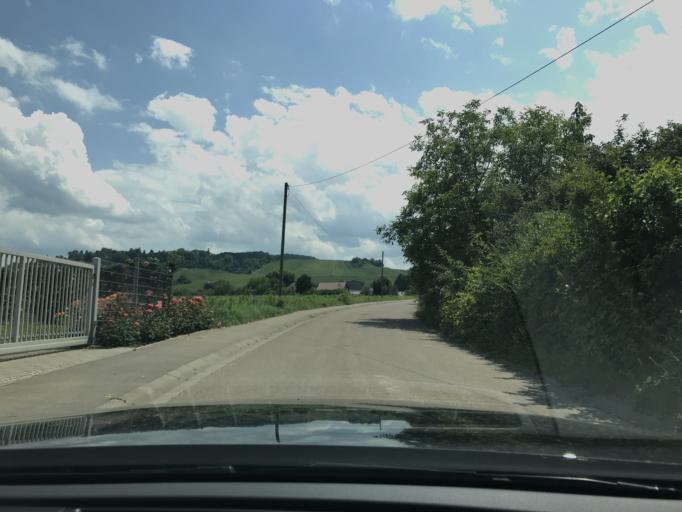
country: DE
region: Baden-Wuerttemberg
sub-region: Regierungsbezirk Stuttgart
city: Weinstadt-Endersbach
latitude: 48.8035
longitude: 9.3680
